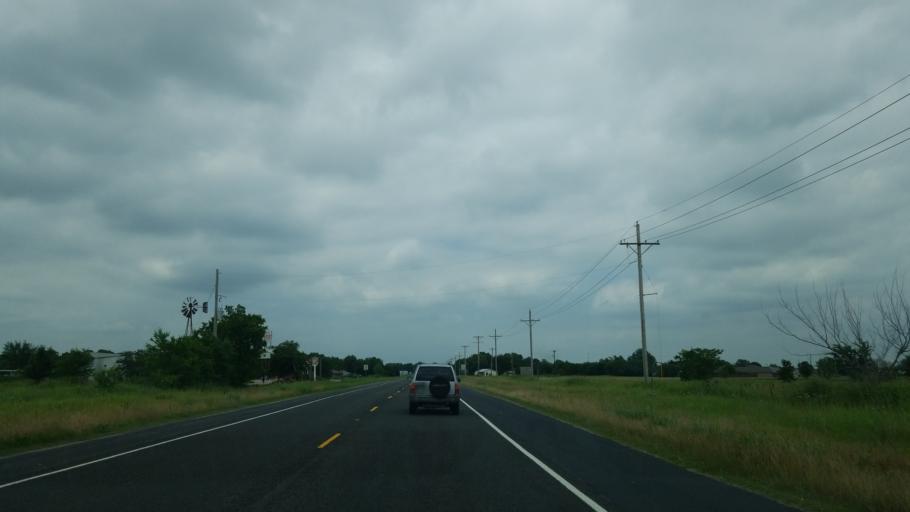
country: US
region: Texas
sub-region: Denton County
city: Pilot Point
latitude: 33.4535
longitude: -96.9212
